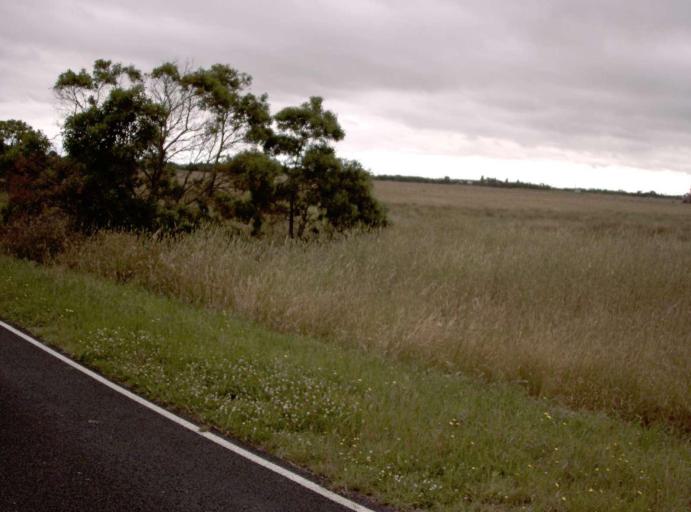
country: AU
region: Victoria
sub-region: Wellington
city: Sale
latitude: -38.5487
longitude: 146.8857
